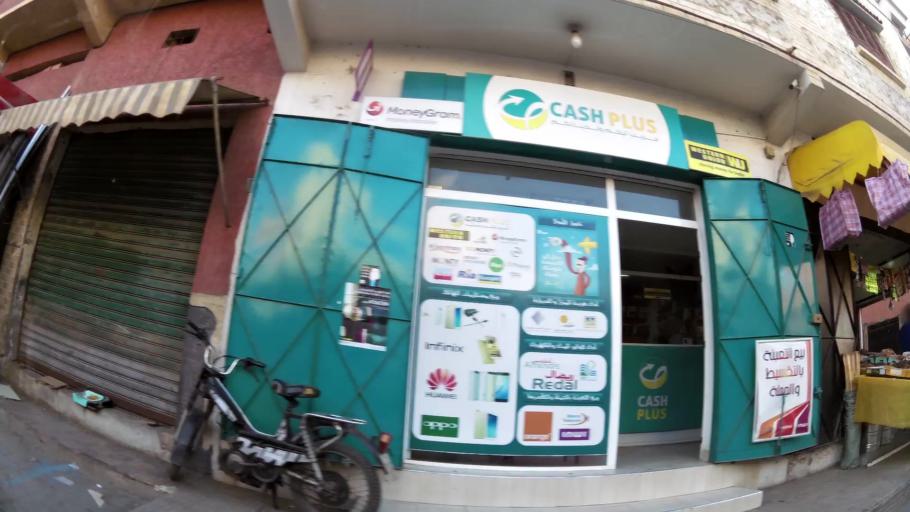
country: MA
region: Rabat-Sale-Zemmour-Zaer
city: Sale
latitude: 34.0537
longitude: -6.7899
